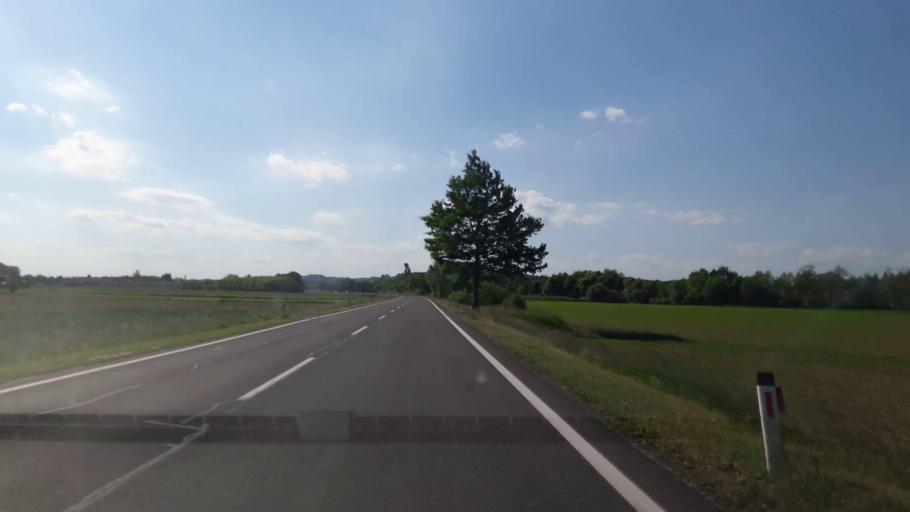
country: AT
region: Styria
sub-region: Politischer Bezirk Suedoststeiermark
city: Fehring
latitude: 46.9394
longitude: 16.0331
